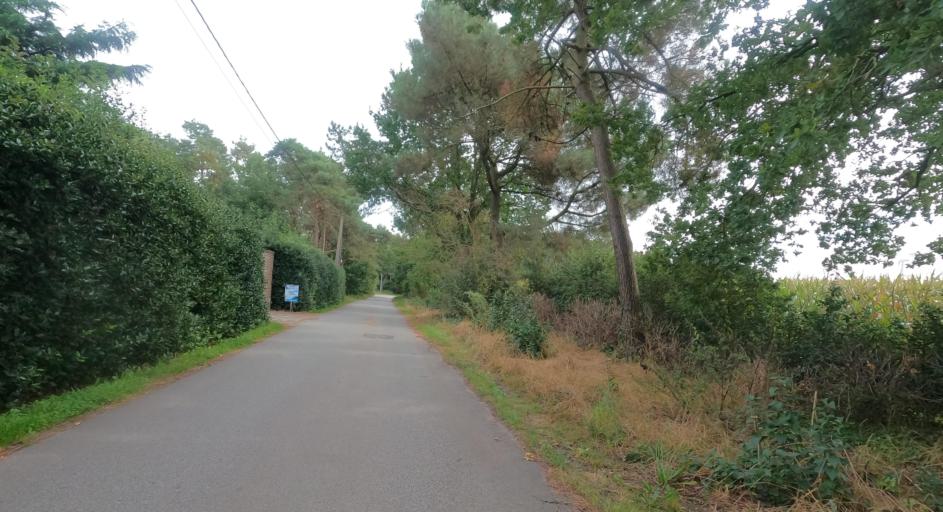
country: BE
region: Flanders
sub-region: Provincie Antwerpen
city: Essen
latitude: 51.4482
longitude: 4.5095
